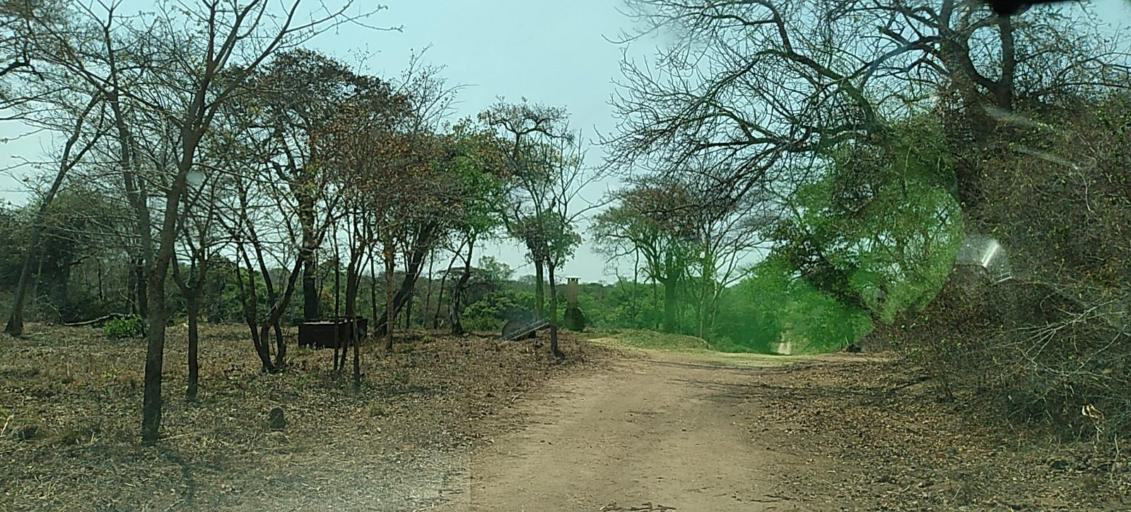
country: ZM
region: North-Western
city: Kalengwa
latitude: -13.1010
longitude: 24.6928
